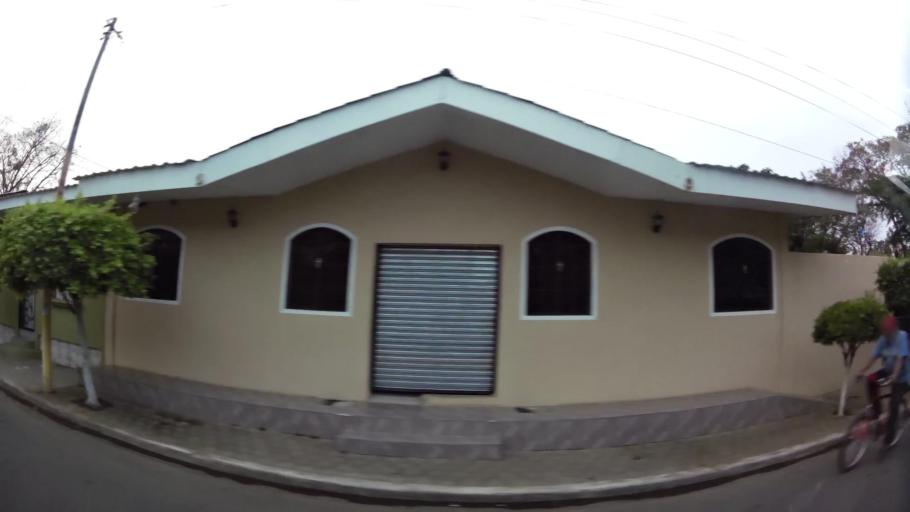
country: NI
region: Masaya
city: Nindiri
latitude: 12.0044
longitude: -86.1227
